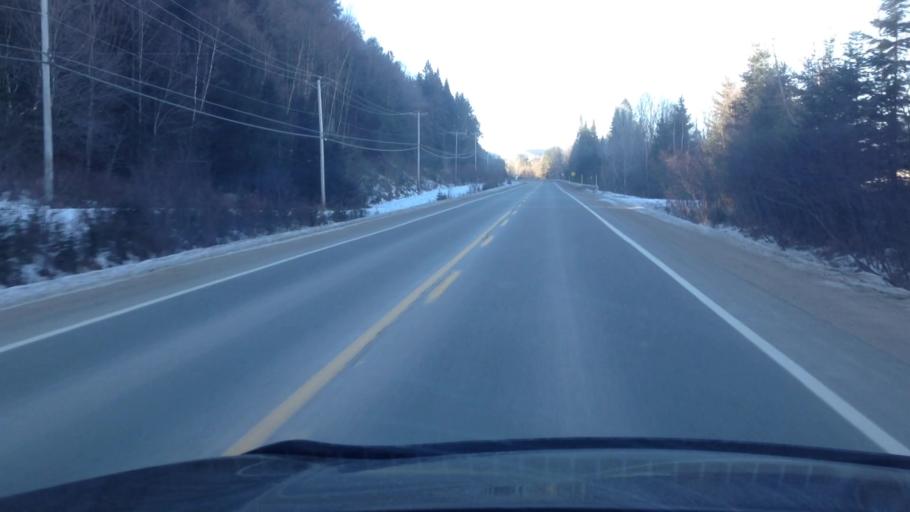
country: CA
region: Quebec
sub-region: Laurentides
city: Mont-Tremblant
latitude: 45.9623
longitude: -74.6068
